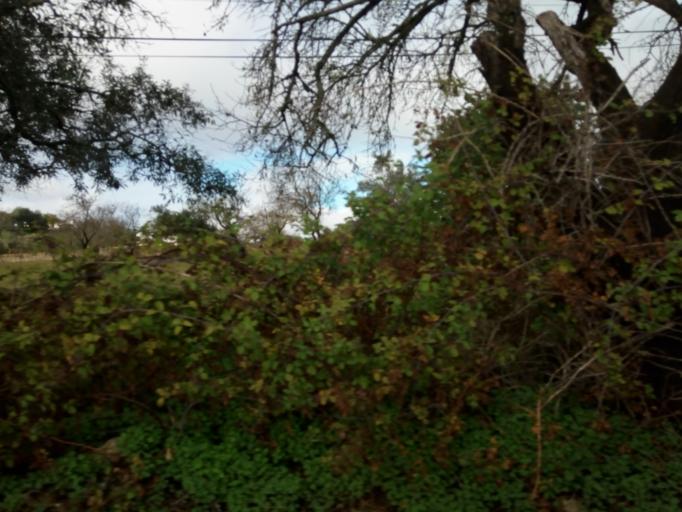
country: PT
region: Faro
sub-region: Faro
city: Santa Barbara de Nexe
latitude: 37.1206
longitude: -7.9573
